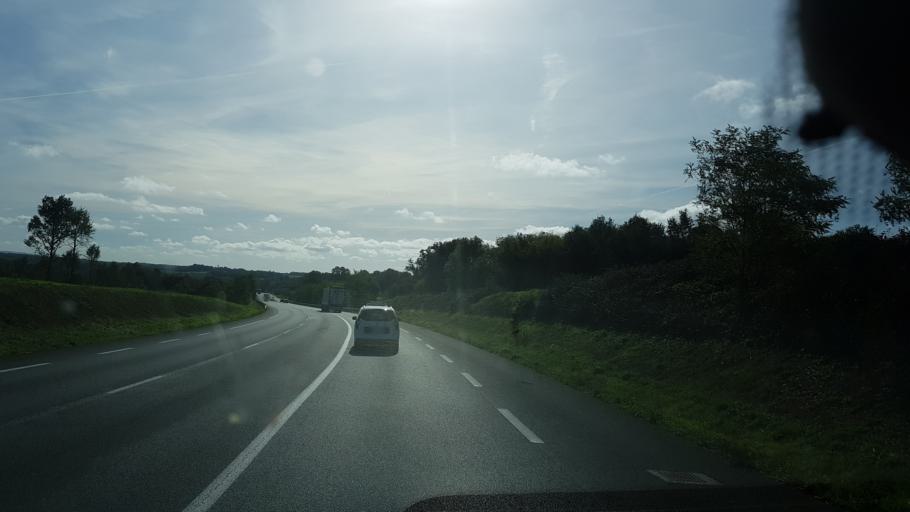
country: FR
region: Poitou-Charentes
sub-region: Departement de la Charente
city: Saint-Claud
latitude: 45.9000
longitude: 0.4793
